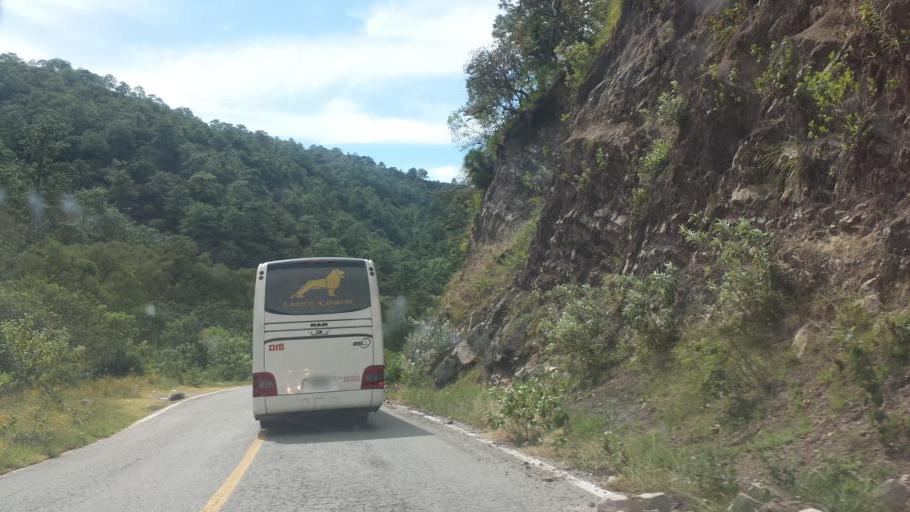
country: MX
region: Oaxaca
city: San Francisco Sola
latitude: 16.4374
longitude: -97.0328
